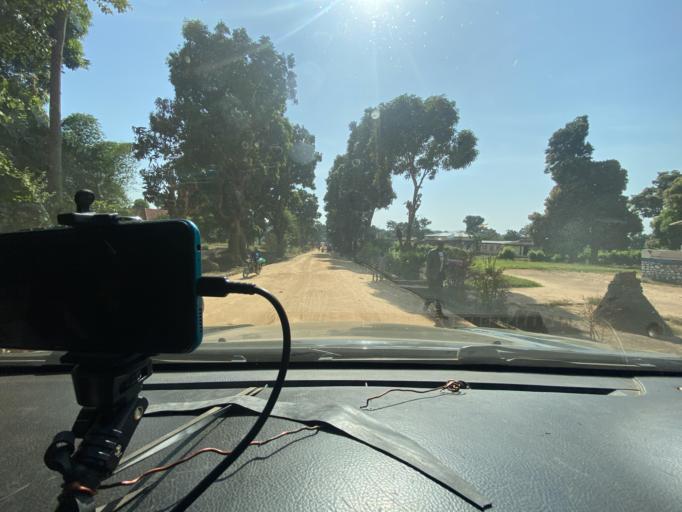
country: CD
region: Kasai-Oriental
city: Kabinda
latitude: -6.1333
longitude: 24.4876
